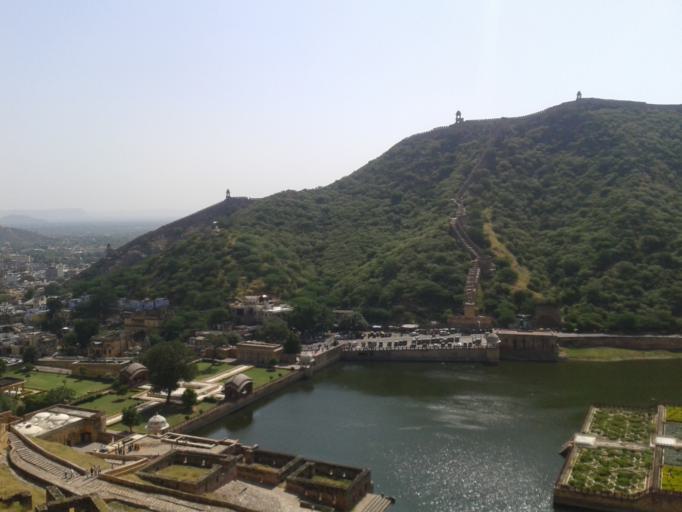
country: IN
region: Rajasthan
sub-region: Jaipur
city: Jaipur
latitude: 26.9860
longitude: 75.8509
